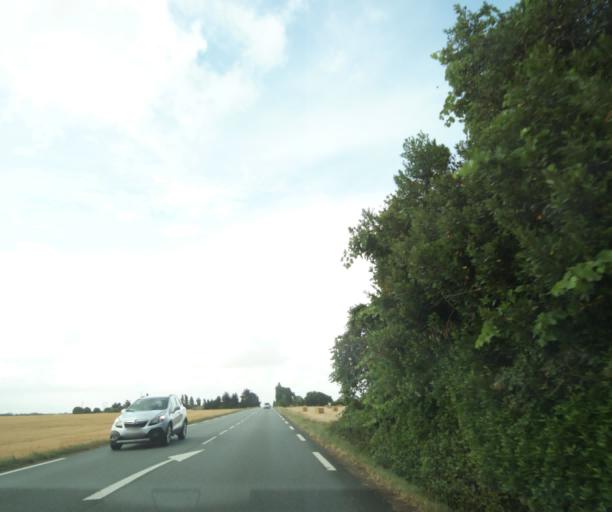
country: FR
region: Poitou-Charentes
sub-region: Departement de la Charente-Maritime
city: Charron
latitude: 46.2981
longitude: -1.0866
